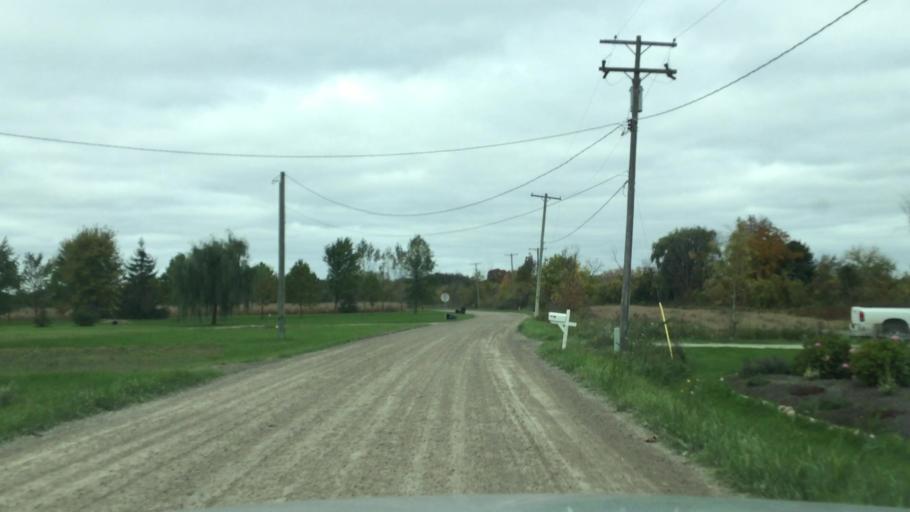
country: US
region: Michigan
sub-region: Macomb County
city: Richmond
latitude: 42.8216
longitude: -82.7391
